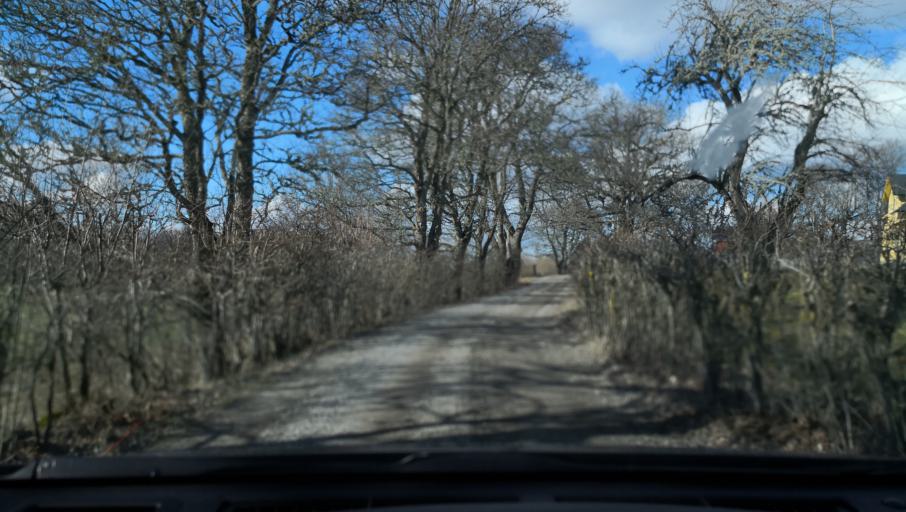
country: SE
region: OErebro
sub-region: Lindesbergs Kommun
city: Fellingsbro
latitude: 59.4179
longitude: 15.6326
